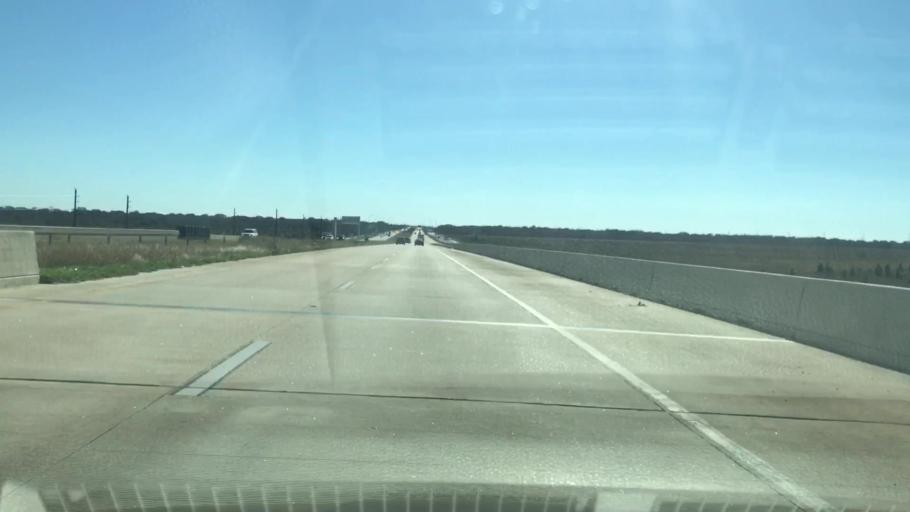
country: US
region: Texas
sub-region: Harris County
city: Cypress
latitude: 29.9775
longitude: -95.7697
